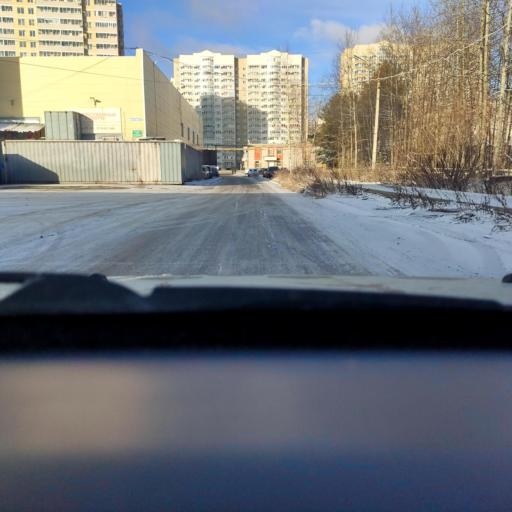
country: RU
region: Perm
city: Kondratovo
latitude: 58.0331
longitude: 56.1439
